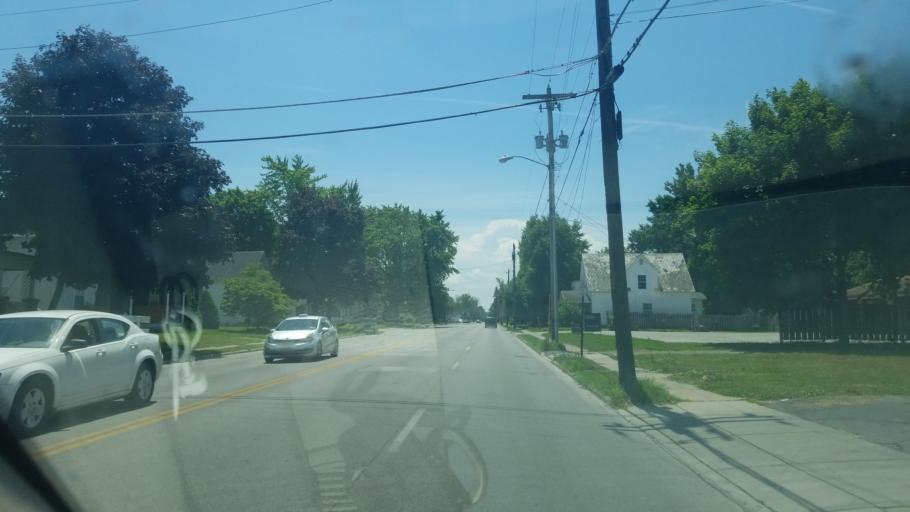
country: US
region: Ohio
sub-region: Hancock County
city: Findlay
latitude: 41.0340
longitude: -83.6412
